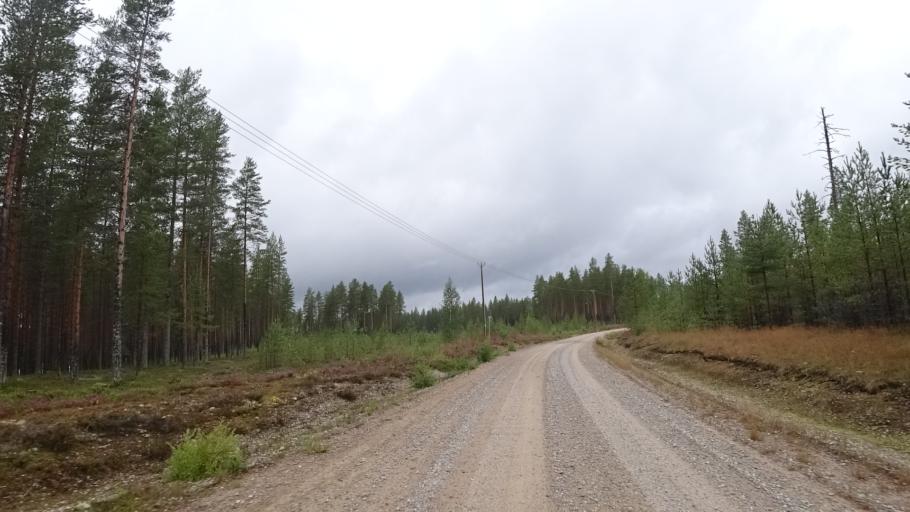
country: FI
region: North Karelia
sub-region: Pielisen Karjala
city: Lieksa
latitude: 63.5321
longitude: 30.0566
